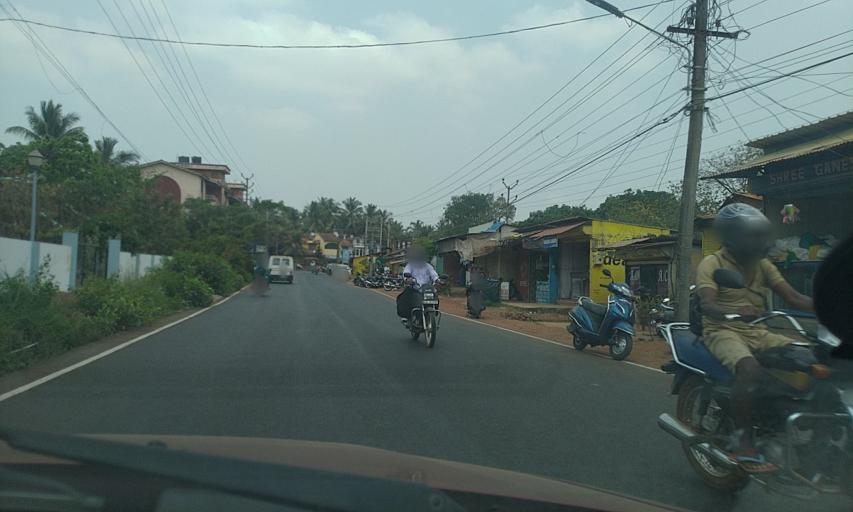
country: IN
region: Goa
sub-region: North Goa
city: Mapuca
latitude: 15.6023
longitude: 73.8058
